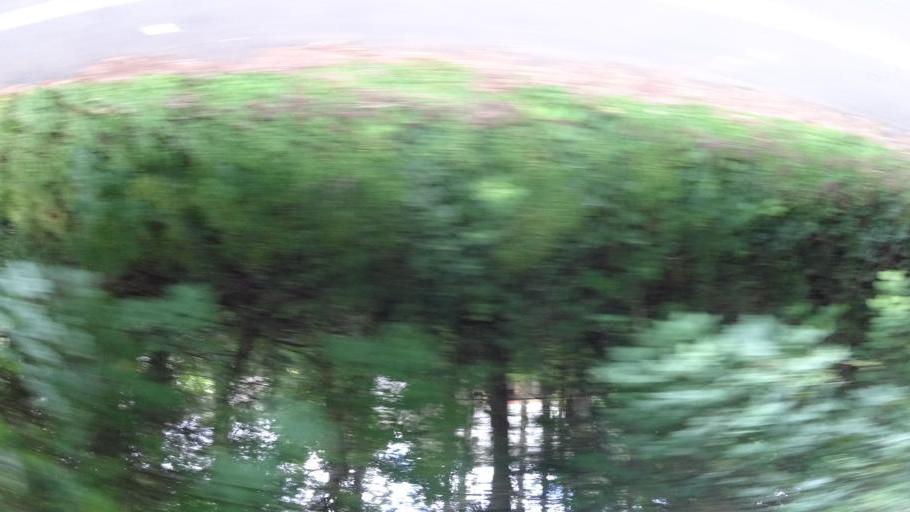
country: US
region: Oregon
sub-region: Clackamas County
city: Lake Oswego
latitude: 45.4423
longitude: -122.6724
